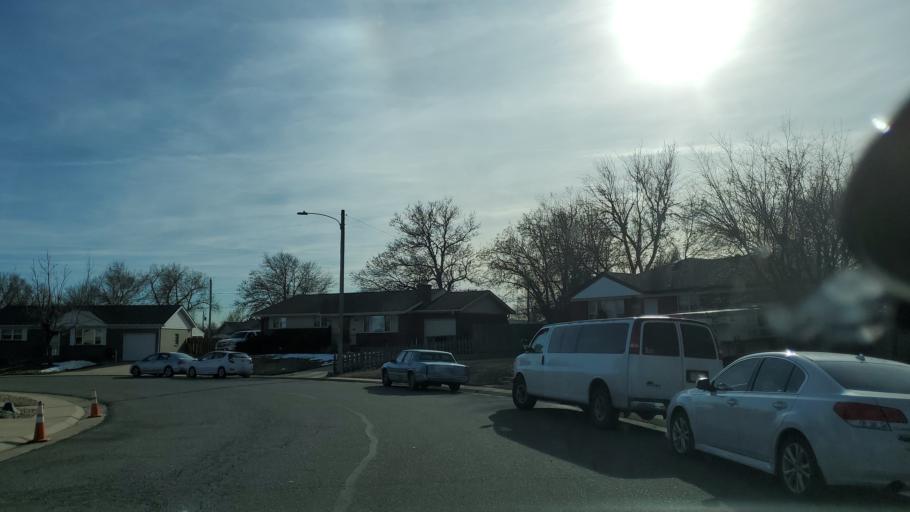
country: US
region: Colorado
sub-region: Adams County
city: Northglenn
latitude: 39.9047
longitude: -104.9640
